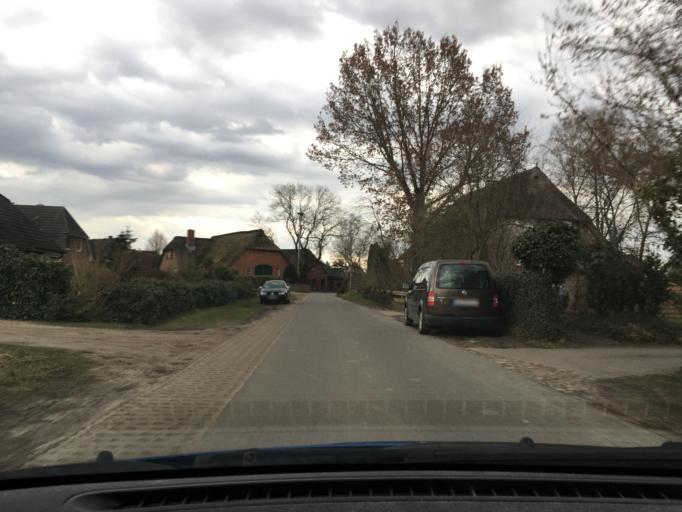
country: DE
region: Lower Saxony
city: Drage
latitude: 53.3716
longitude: 10.2628
